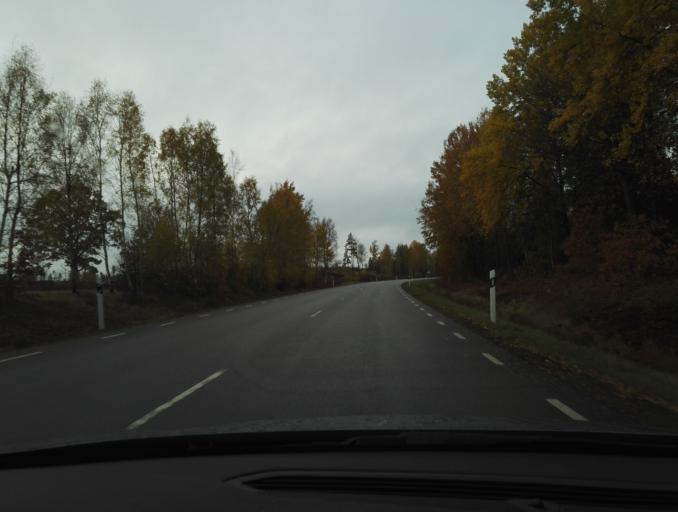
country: SE
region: Kronoberg
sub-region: Vaxjo Kommun
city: Vaexjoe
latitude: 56.9146
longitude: 14.7293
